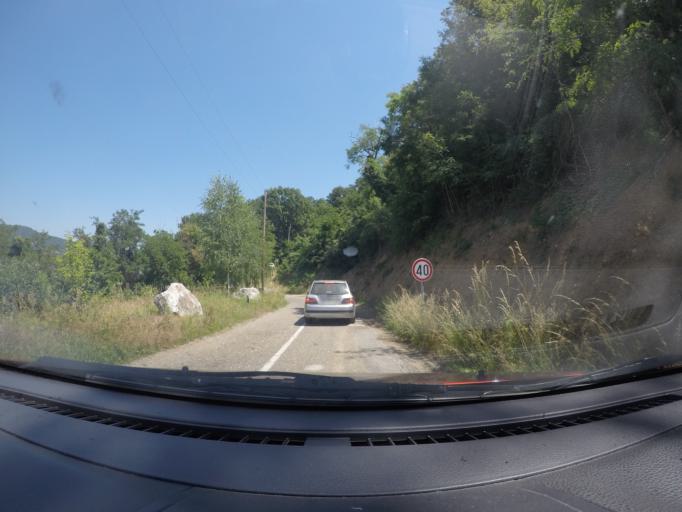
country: RO
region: Mehedinti
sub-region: Comuna Svinita
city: Svinita
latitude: 44.4742
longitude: 22.1057
